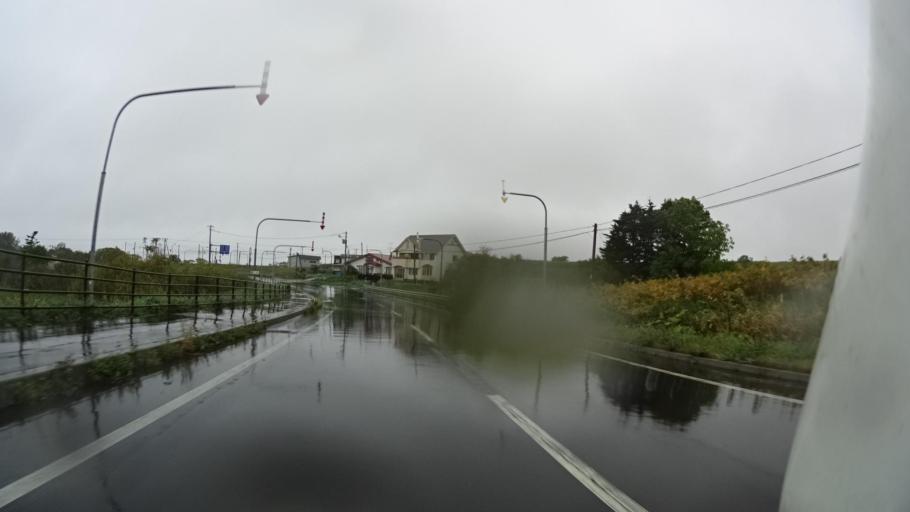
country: JP
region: Hokkaido
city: Nemuro
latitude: 43.2811
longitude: 145.5086
